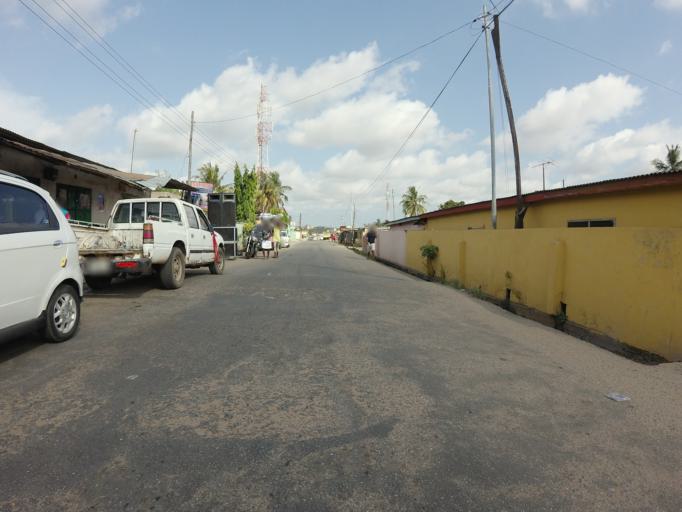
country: GH
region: Greater Accra
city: Dome
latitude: 5.6150
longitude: -0.2357
